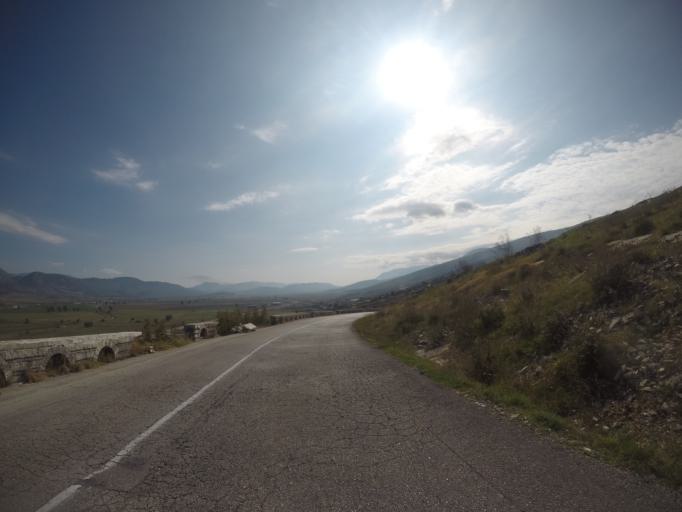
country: AL
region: Gjirokaster
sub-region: Rrethi i Gjirokastres
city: Libohove
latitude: 39.9428
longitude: 20.2602
